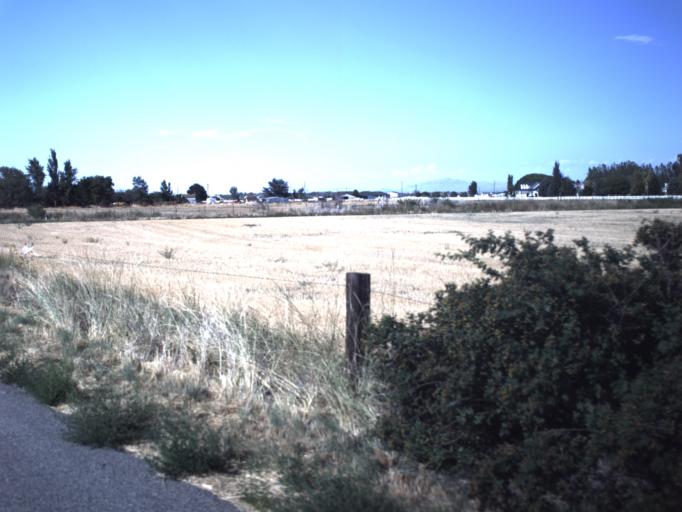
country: US
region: Utah
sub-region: Tooele County
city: Grantsville
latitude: 40.5946
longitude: -112.4255
